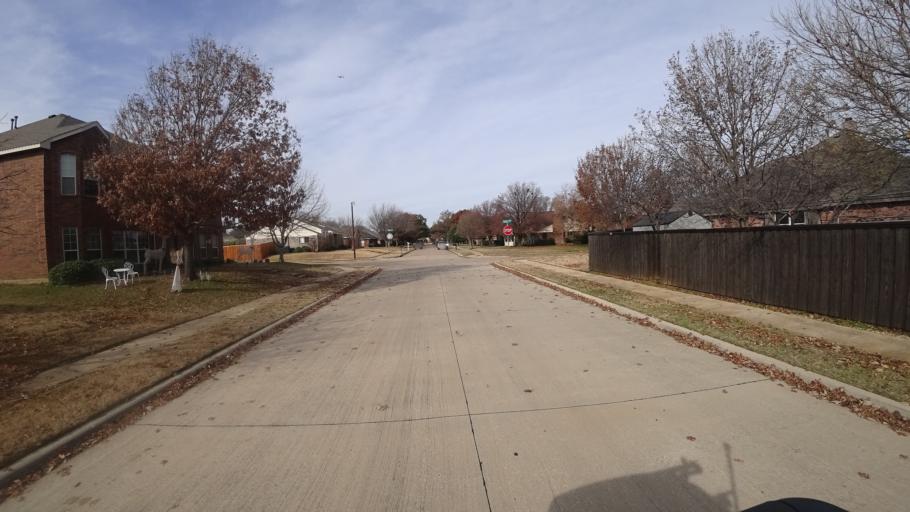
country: US
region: Texas
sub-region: Denton County
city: Highland Village
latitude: 33.0753
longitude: -97.0377
